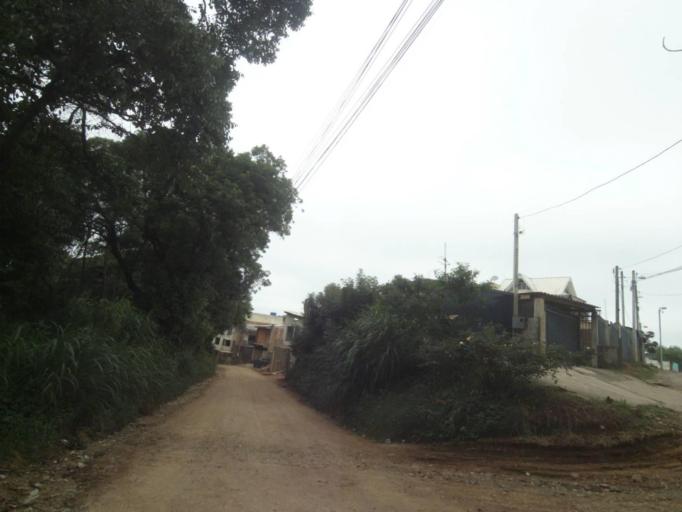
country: BR
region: Parana
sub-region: Curitiba
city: Curitiba
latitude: -25.5028
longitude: -49.3492
